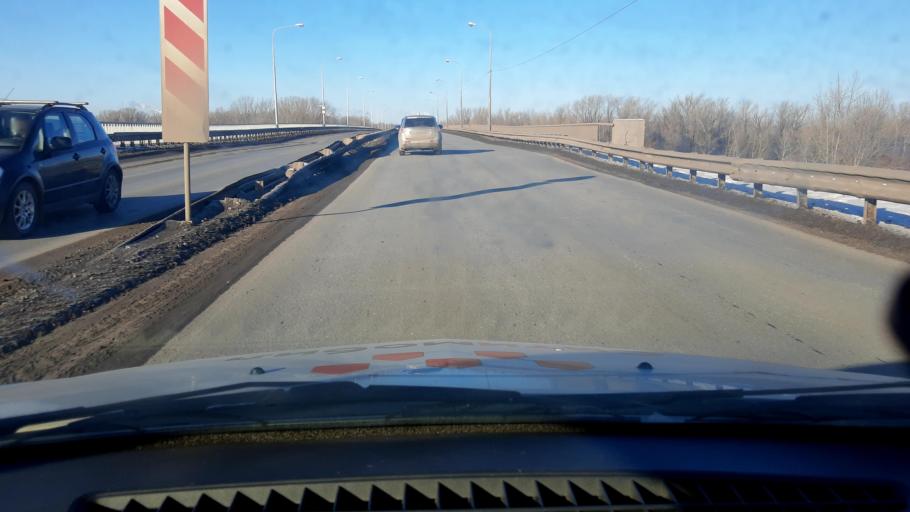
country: RU
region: Bashkortostan
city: Iglino
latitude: 54.7857
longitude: 56.2204
